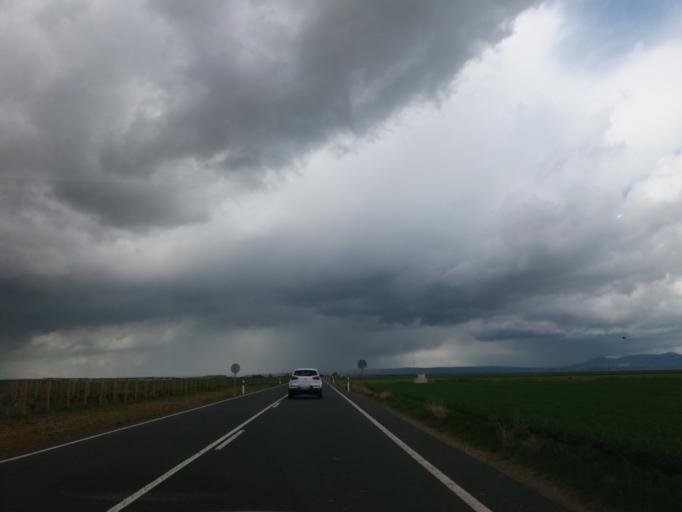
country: ES
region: La Rioja
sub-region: Provincia de La Rioja
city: Rodezno
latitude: 42.5436
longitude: -2.8675
